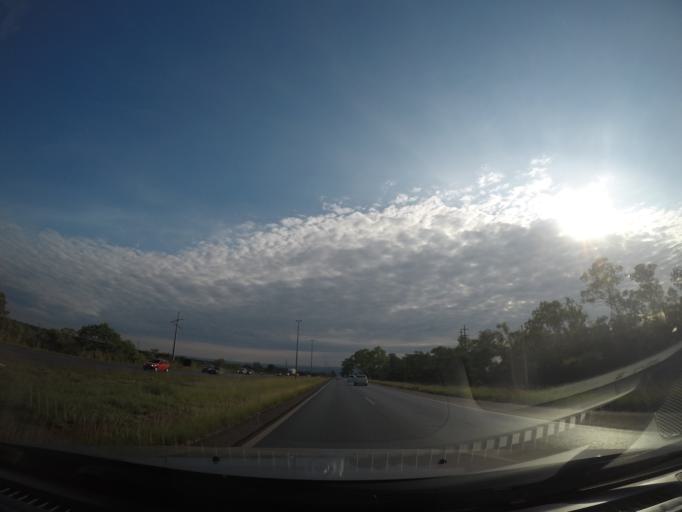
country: BR
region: Goias
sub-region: Planaltina
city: Planaltina
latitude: -15.6284
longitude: -47.7296
